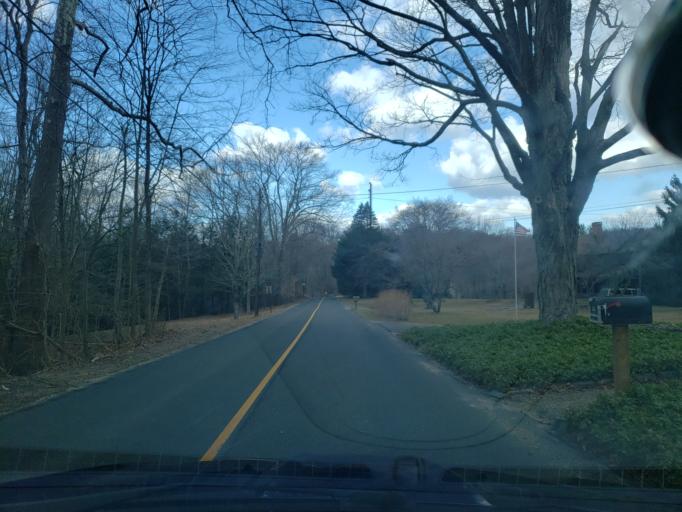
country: US
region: Connecticut
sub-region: Fairfield County
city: Bethel
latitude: 41.3900
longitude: -73.3850
